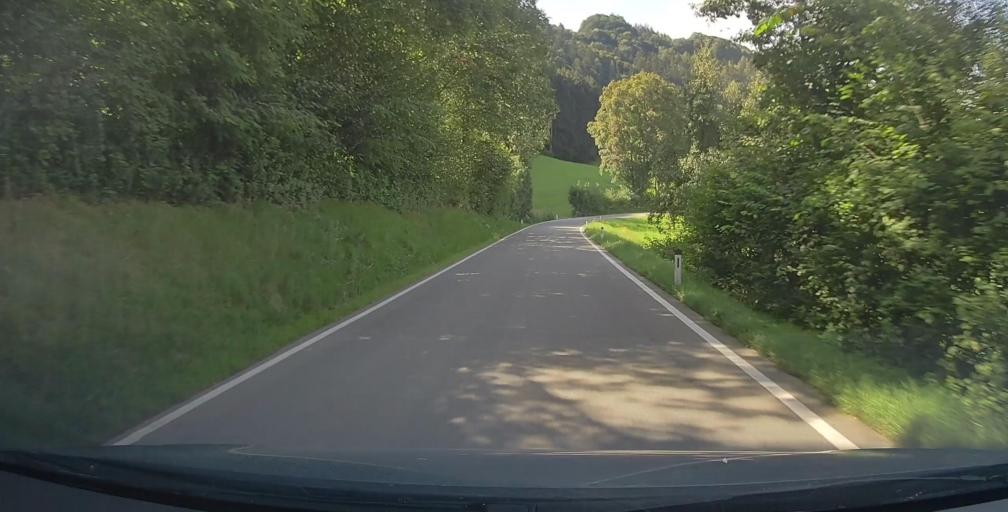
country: AT
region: Tyrol
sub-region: Politischer Bezirk Schwaz
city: Buch bei Jenbach
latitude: 47.3697
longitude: 11.7477
